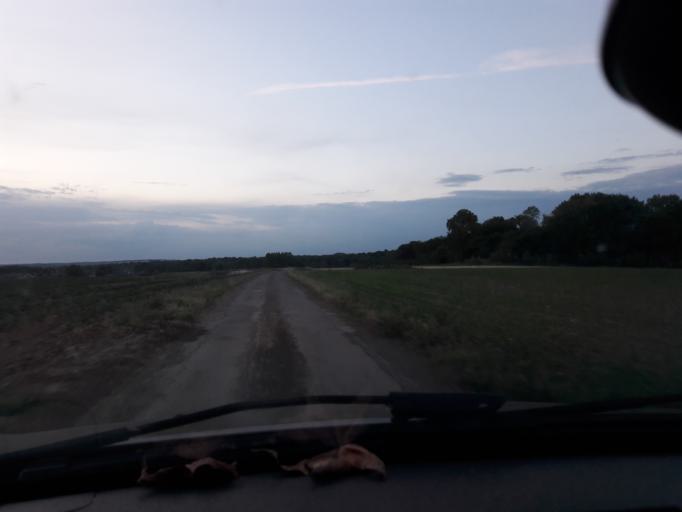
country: BE
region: Wallonia
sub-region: Province du Hainaut
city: Merbes-le-Chateau
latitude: 50.2746
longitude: 4.1943
